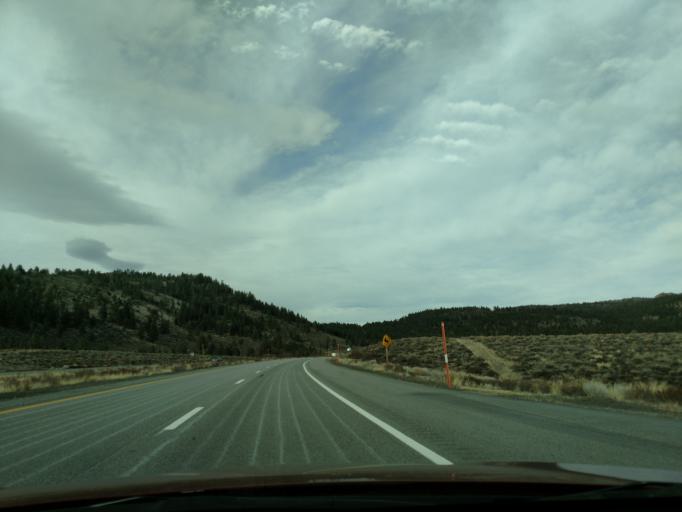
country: US
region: California
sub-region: Mono County
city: Mammoth Lakes
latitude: 37.6465
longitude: -118.9231
